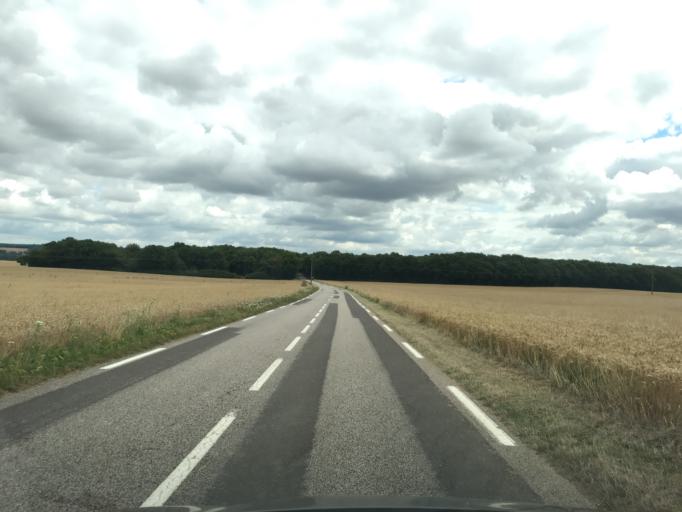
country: FR
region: Haute-Normandie
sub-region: Departement de l'Eure
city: Menilles
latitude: 49.0375
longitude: 1.2984
